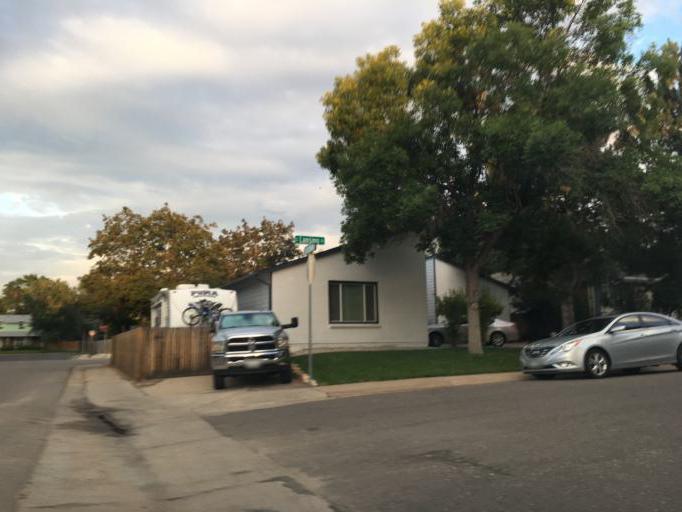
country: US
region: Colorado
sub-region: Adams County
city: Aurora
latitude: 39.6802
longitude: -104.8573
